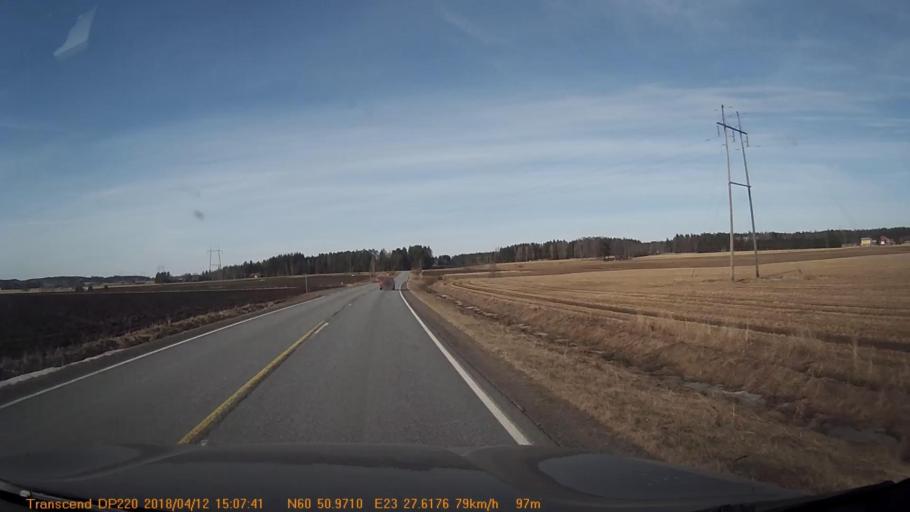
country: FI
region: Haeme
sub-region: Forssa
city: Jokioinen
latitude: 60.8501
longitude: 23.4602
